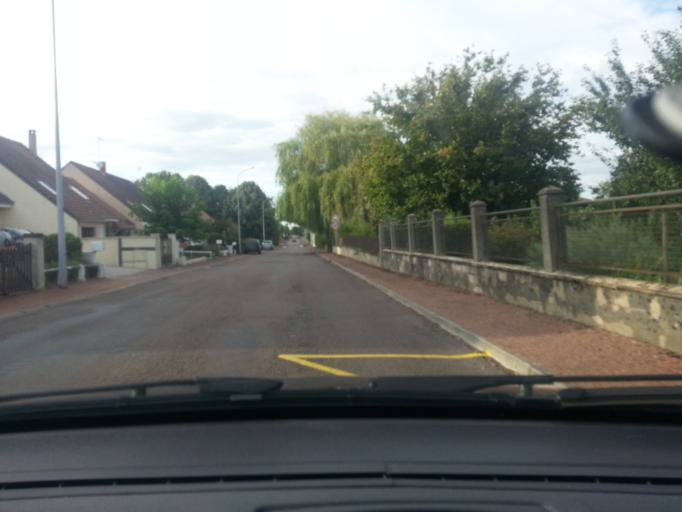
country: FR
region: Bourgogne
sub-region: Departement de Saone-et-Loire
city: Chatenoy-le-Royal
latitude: 46.7990
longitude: 4.8041
